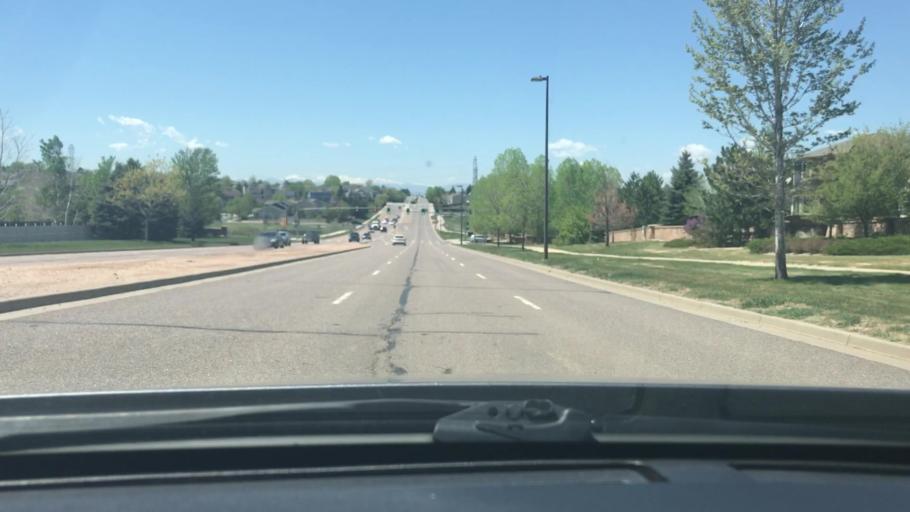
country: US
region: Colorado
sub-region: Arapahoe County
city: Dove Valley
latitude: 39.6531
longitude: -104.7483
